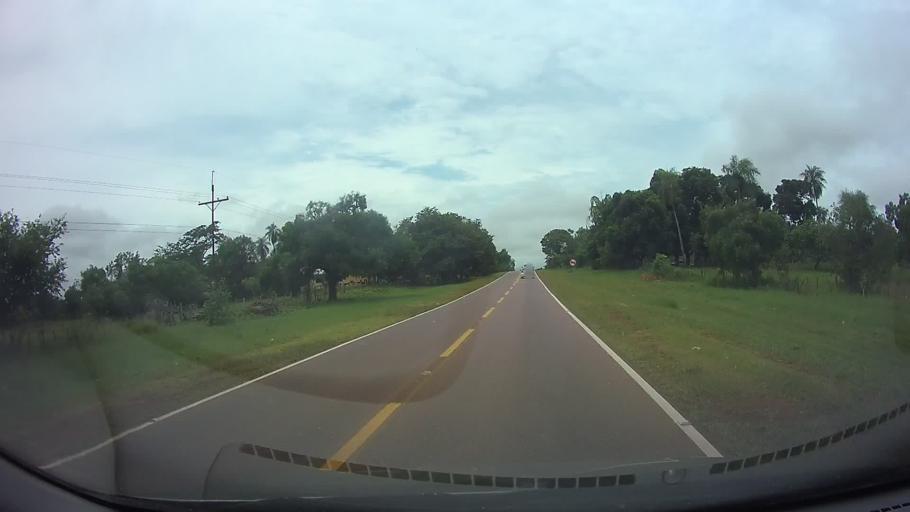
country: PY
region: Paraguari
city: Acahay
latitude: -25.8485
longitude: -57.1436
